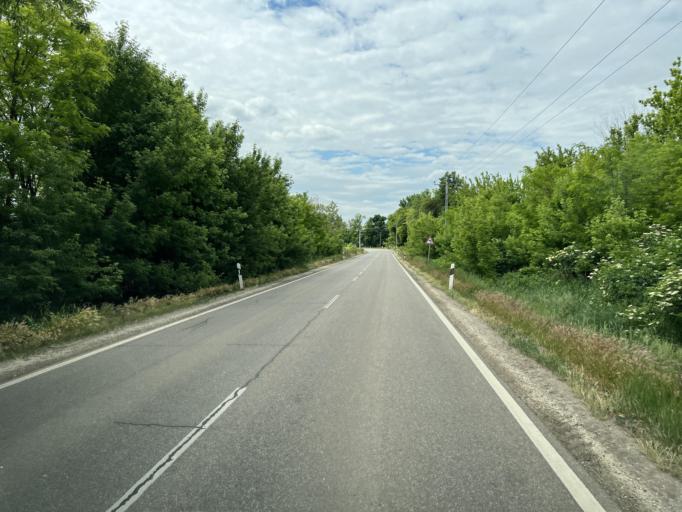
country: HU
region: Pest
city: Koka
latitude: 47.4977
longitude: 19.5852
